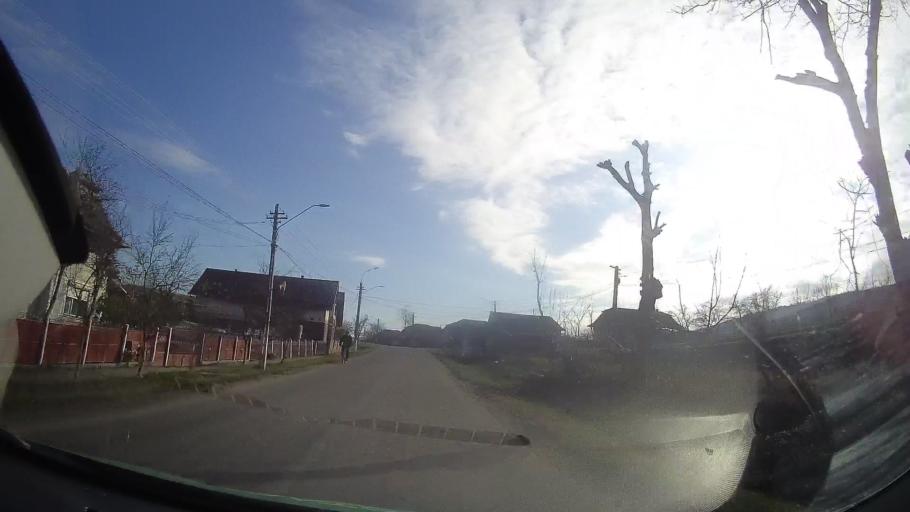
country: RO
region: Mures
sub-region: Comuna Valea Larga
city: Valea Larga
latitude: 46.6166
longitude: 24.0816
